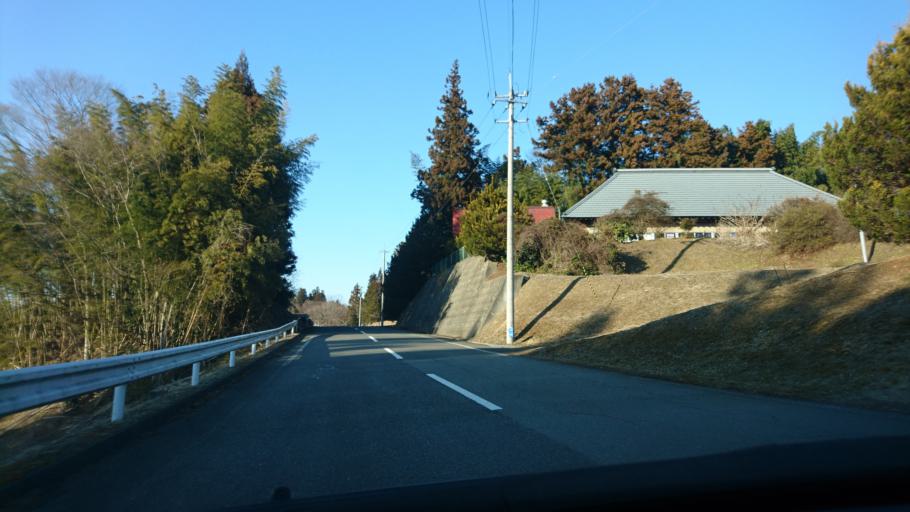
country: JP
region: Iwate
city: Ichinoseki
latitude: 38.8782
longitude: 141.3902
